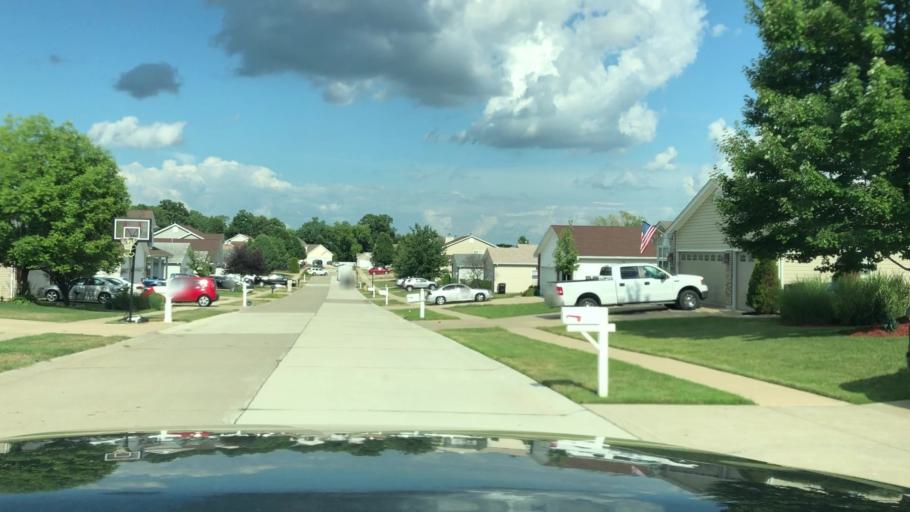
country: US
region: Missouri
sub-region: Saint Charles County
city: Wentzville
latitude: 38.8390
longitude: -90.8866
